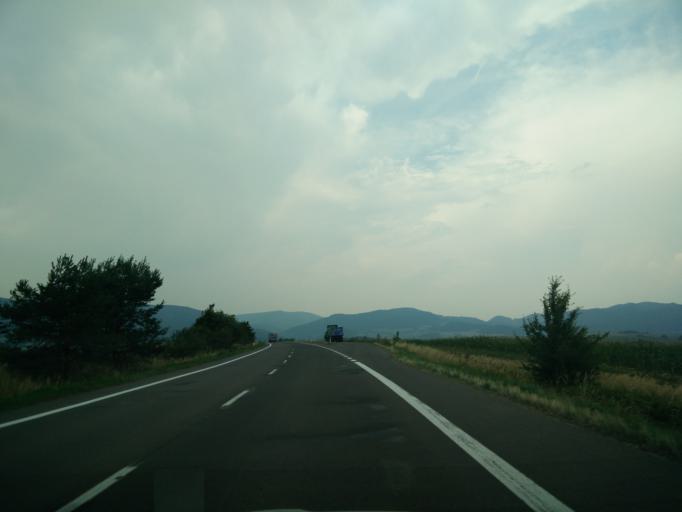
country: SK
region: Banskobystricky
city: Ziar nad Hronom
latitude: 48.6168
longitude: 18.8137
